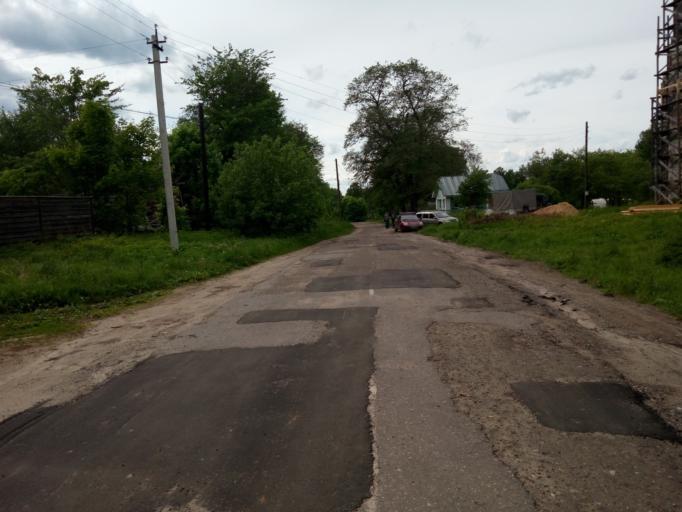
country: RU
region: Nizjnij Novgorod
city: Voskresenskoye
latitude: 56.7793
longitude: 45.5365
